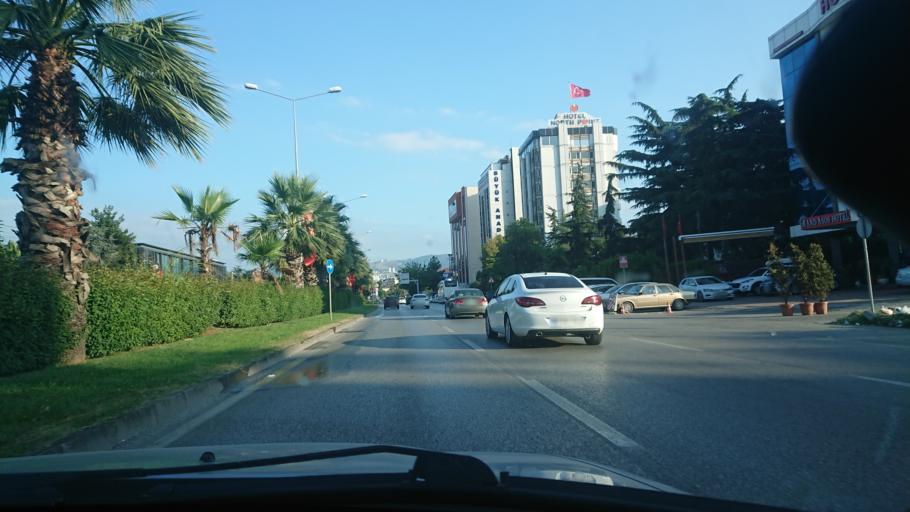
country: TR
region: Samsun
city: Samsun
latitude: 41.2936
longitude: 36.3341
